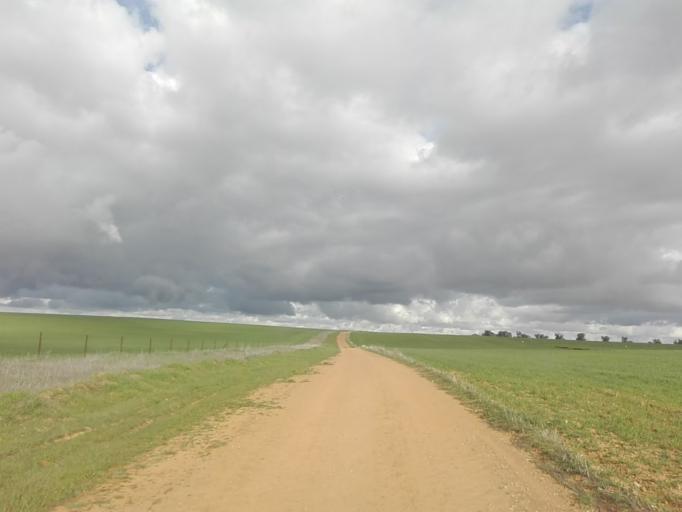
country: ES
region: Extremadura
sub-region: Provincia de Badajoz
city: Llerena
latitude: 38.2858
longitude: -6.0151
